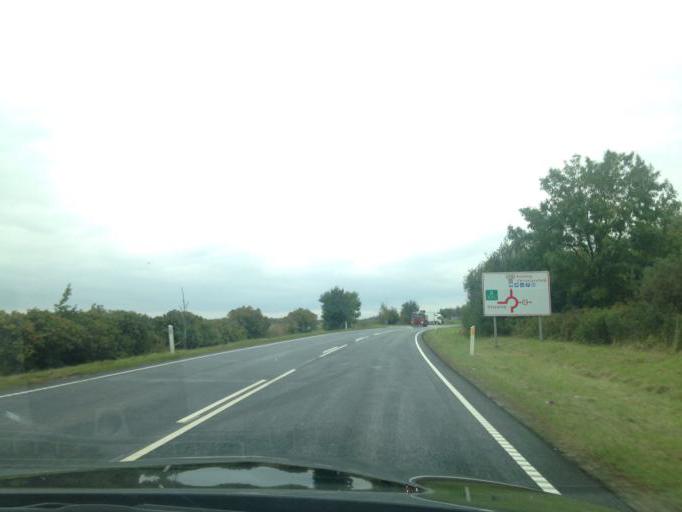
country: DK
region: South Denmark
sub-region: Kolding Kommune
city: Christiansfeld
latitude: 55.3522
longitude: 9.4774
